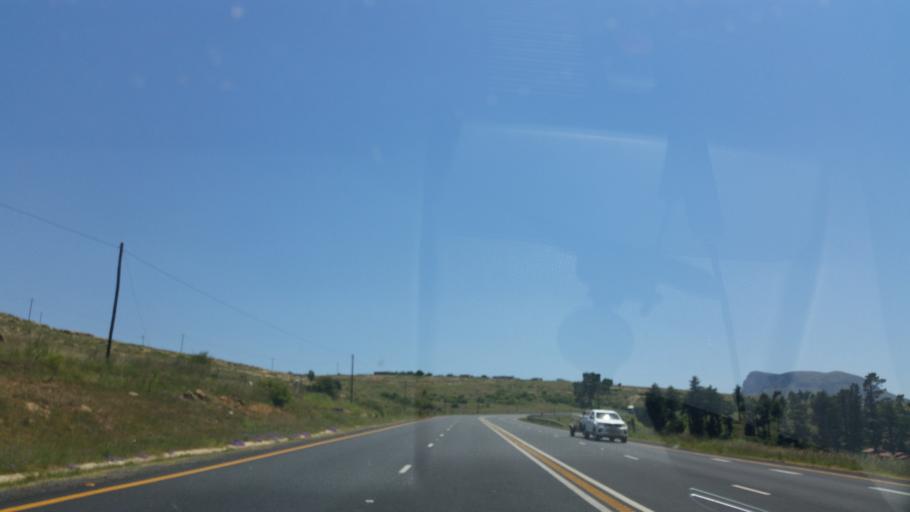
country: ZA
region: Orange Free State
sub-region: Thabo Mofutsanyana District Municipality
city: Harrismith
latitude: -28.2518
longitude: 29.1141
